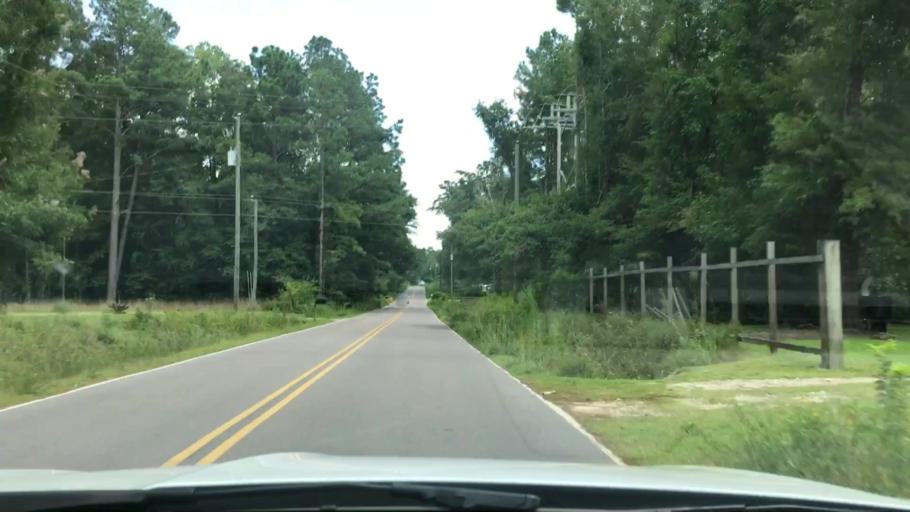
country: US
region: South Carolina
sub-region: Dorchester County
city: Summerville
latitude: 33.0354
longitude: -80.2141
